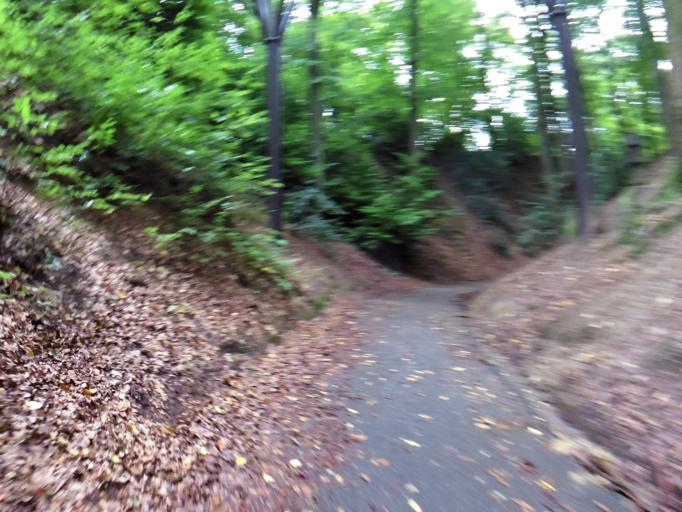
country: NL
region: Limburg
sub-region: Gemeente Heerlen
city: Heerlen
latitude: 50.8866
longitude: 5.9889
